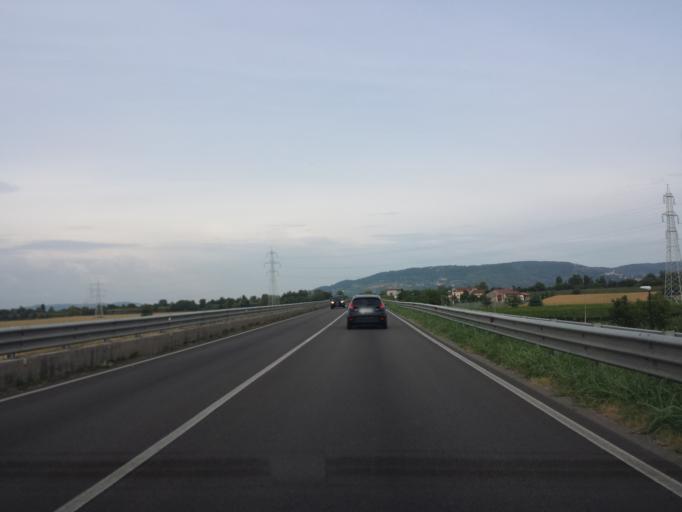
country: IT
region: Veneto
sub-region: Provincia di Vicenza
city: Montebello Vicentino
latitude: 45.4590
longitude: 11.3933
